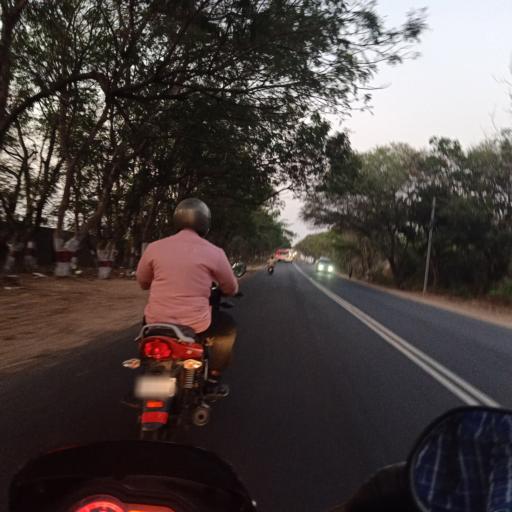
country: IN
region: Telangana
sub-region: Rangareddi
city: Secunderabad
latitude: 17.5495
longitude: 78.5357
